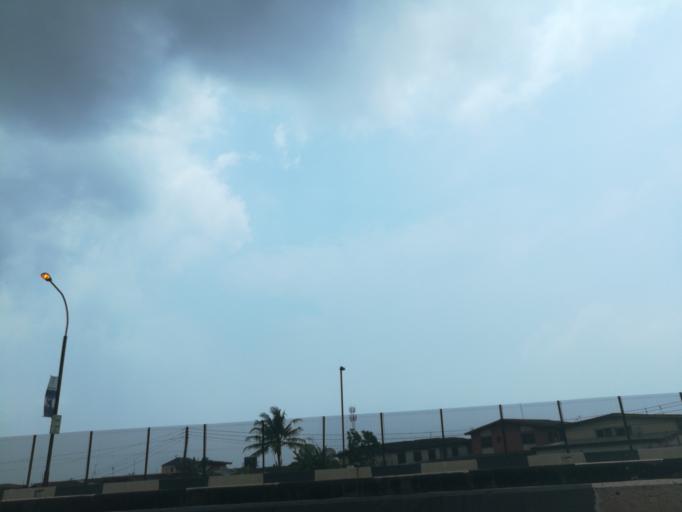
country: NG
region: Lagos
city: Somolu
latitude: 6.5566
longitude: 3.3963
